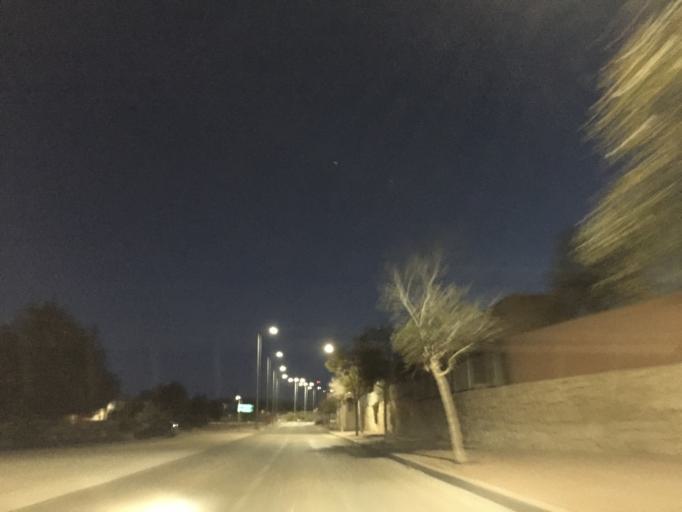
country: IL
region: Southern District
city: Mitzpe Ramon
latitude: 30.6203
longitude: 34.7994
